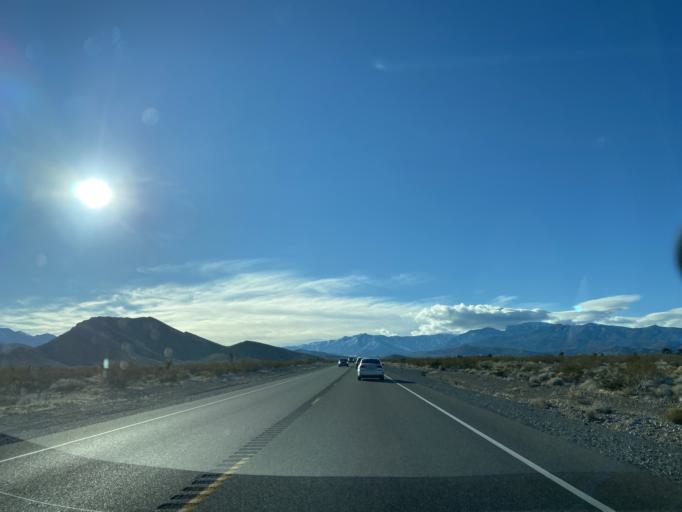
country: US
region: Nevada
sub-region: Clark County
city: Summerlin South
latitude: 36.3126
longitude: -115.3827
